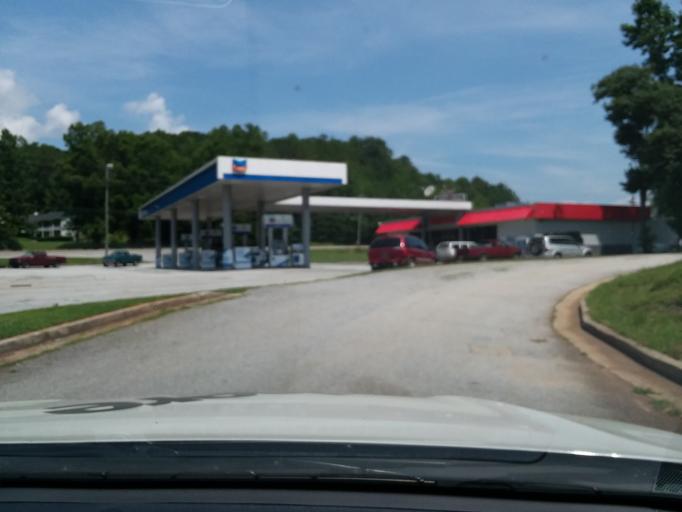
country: US
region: Georgia
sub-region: Rabun County
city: Mountain City
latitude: 34.9845
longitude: -83.3839
